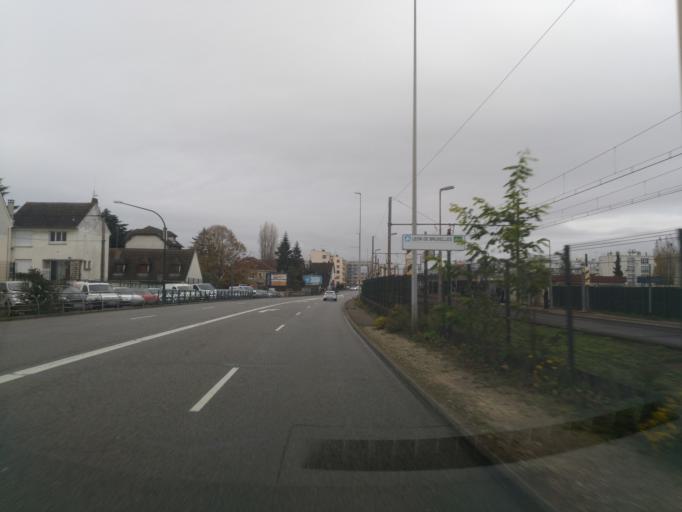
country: FR
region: Ile-de-France
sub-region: Departement des Yvelines
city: Villepreux
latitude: 48.8230
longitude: 1.9937
